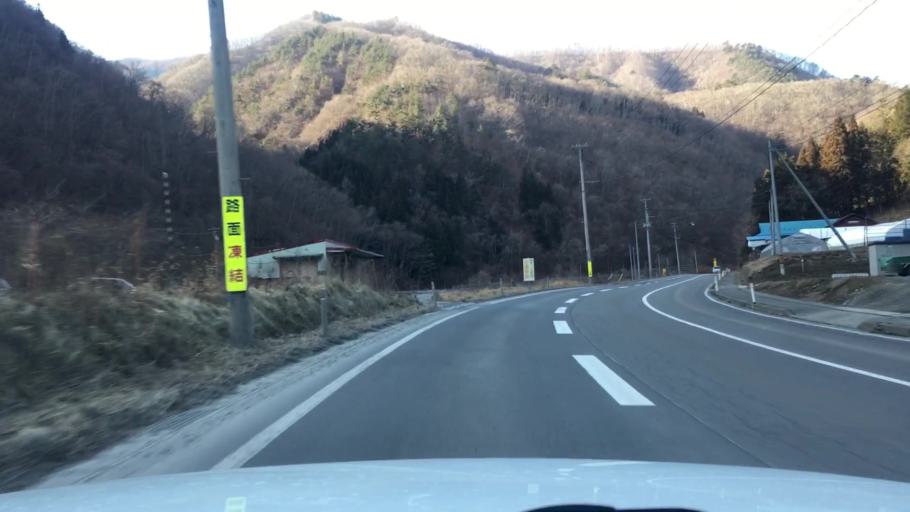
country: JP
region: Iwate
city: Miyako
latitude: 39.5965
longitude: 141.6507
